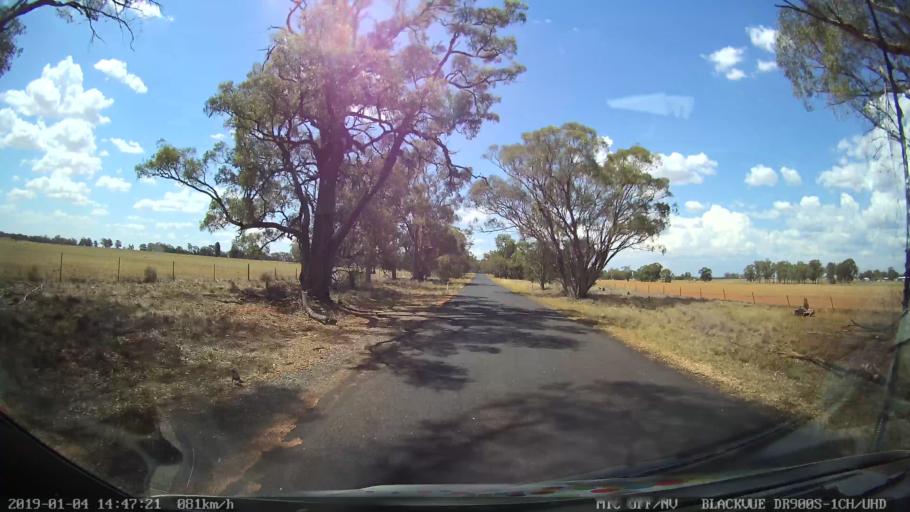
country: AU
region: New South Wales
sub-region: Dubbo Municipality
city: Dubbo
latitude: -32.0701
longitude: 148.6600
